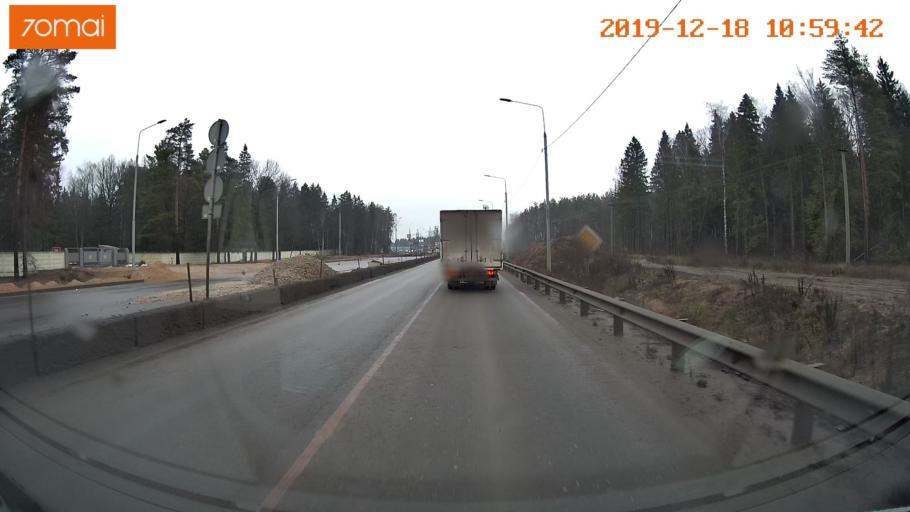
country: RU
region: Moskovskaya
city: Golitsyno
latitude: 55.5625
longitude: 36.9943
